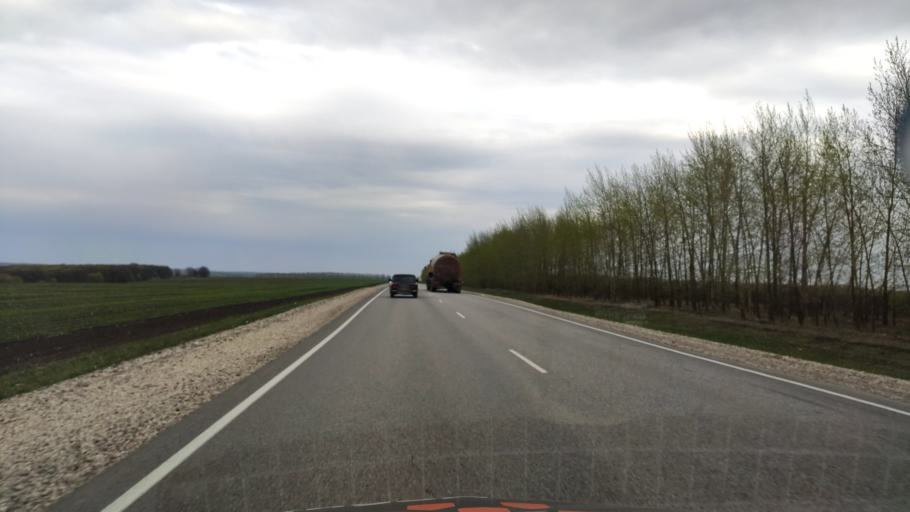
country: RU
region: Voronezj
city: Nizhnedevitsk
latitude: 51.5847
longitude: 38.5260
